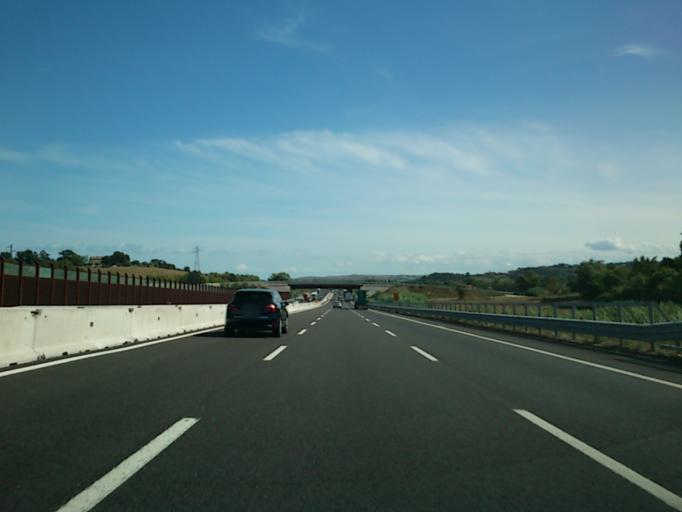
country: IT
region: The Marches
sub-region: Provincia di Pesaro e Urbino
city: Fenile
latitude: 43.8476
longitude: 12.9645
